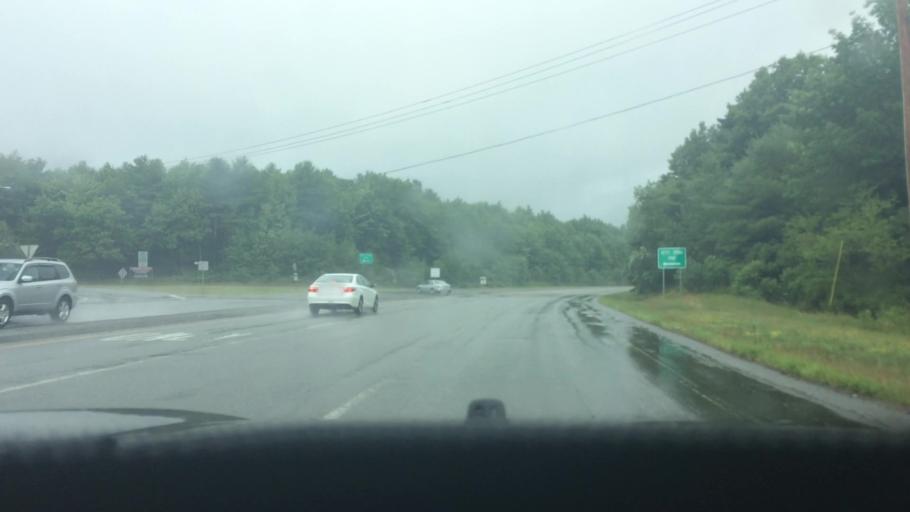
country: US
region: Massachusetts
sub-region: Worcester County
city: Westminster
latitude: 42.5651
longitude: -71.9438
